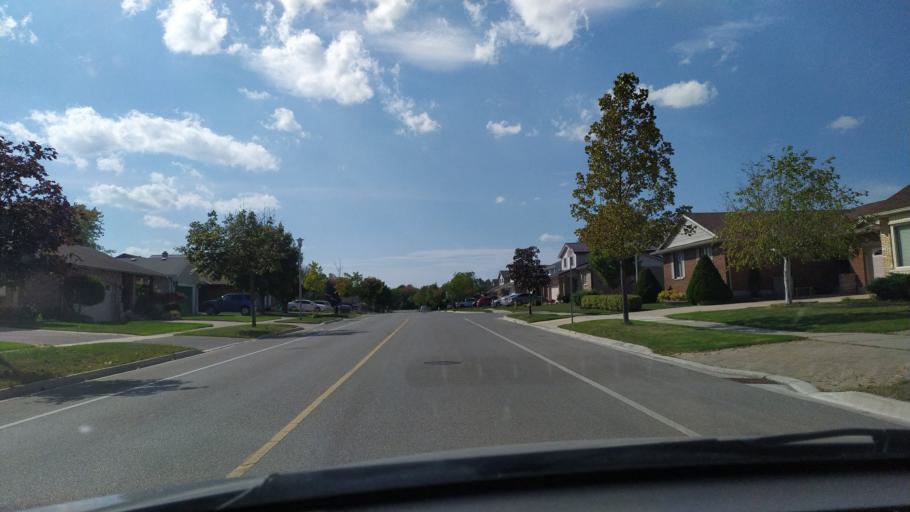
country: CA
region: Ontario
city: London
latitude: 42.9472
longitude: -81.2476
